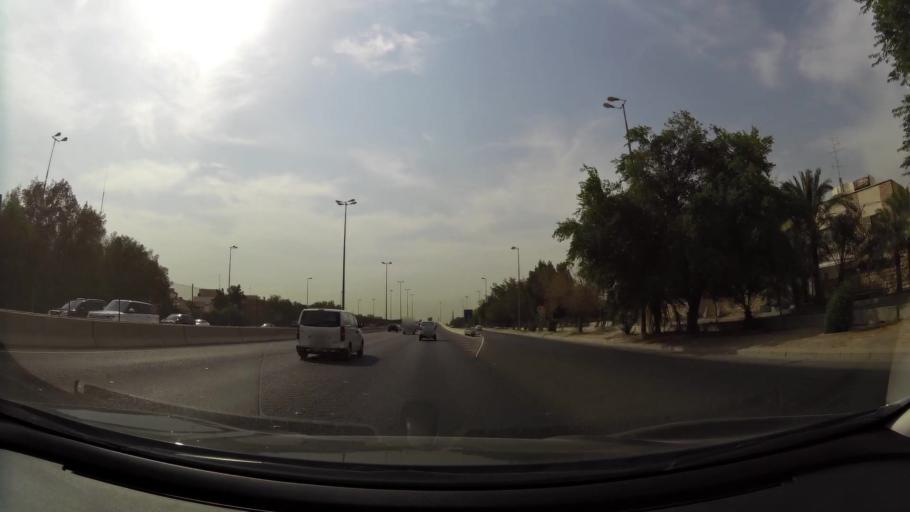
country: KW
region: Al Asimah
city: Ash Shamiyah
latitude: 29.3474
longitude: 47.9728
